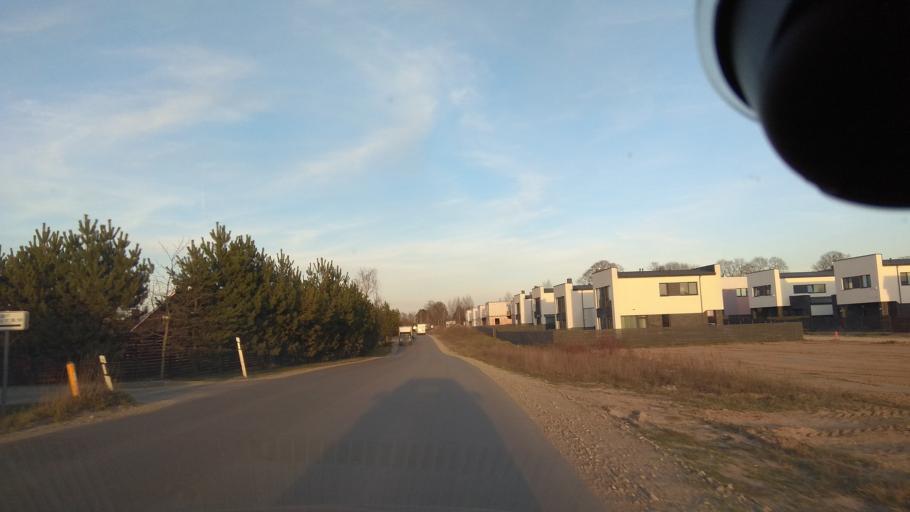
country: LT
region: Vilnius County
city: Pasilaiciai
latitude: 54.7579
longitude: 25.2250
